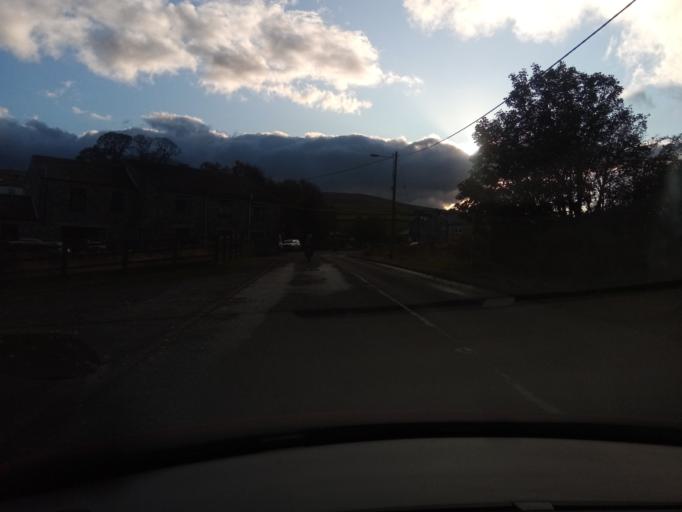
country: GB
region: England
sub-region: County Durham
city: Newbiggin
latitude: 54.7368
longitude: -2.1642
